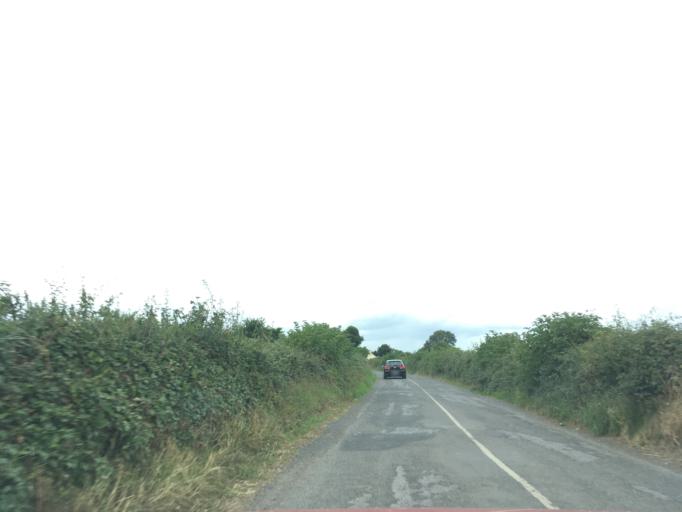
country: IE
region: Munster
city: Cahir
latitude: 52.4581
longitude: -7.9723
